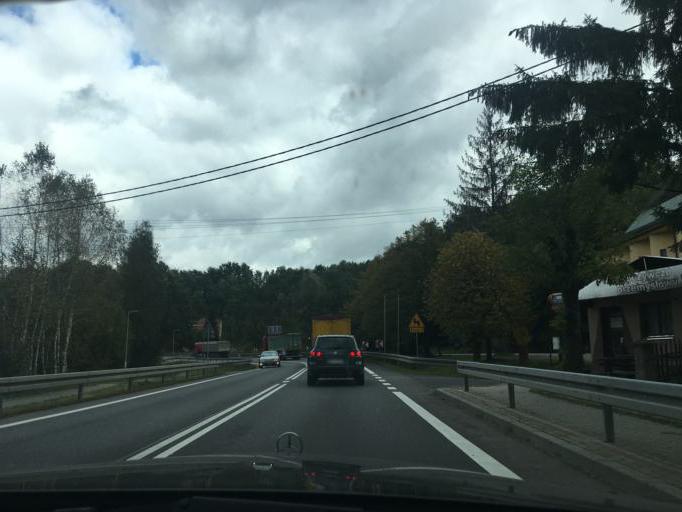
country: PL
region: Subcarpathian Voivodeship
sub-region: Powiat strzyzowski
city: Babica
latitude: 49.9205
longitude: 21.8795
